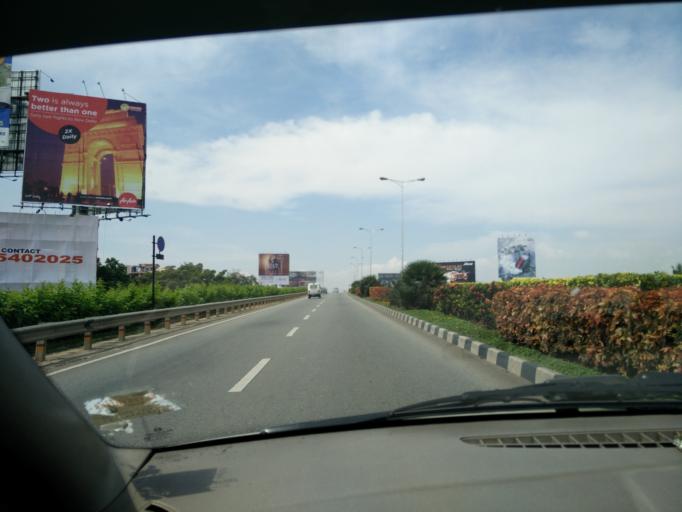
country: IN
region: Karnataka
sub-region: Bangalore Rural
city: Devanhalli
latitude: 13.1981
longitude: 77.6763
